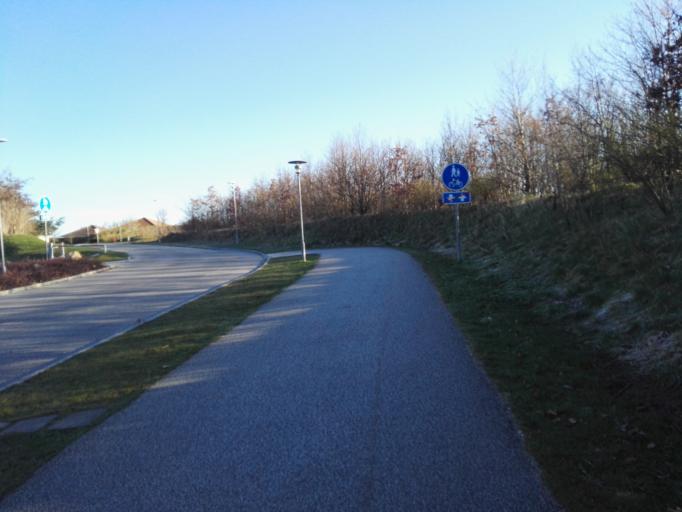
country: DK
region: Capital Region
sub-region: Egedal Kommune
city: Stenlose
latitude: 55.7805
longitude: 12.1846
